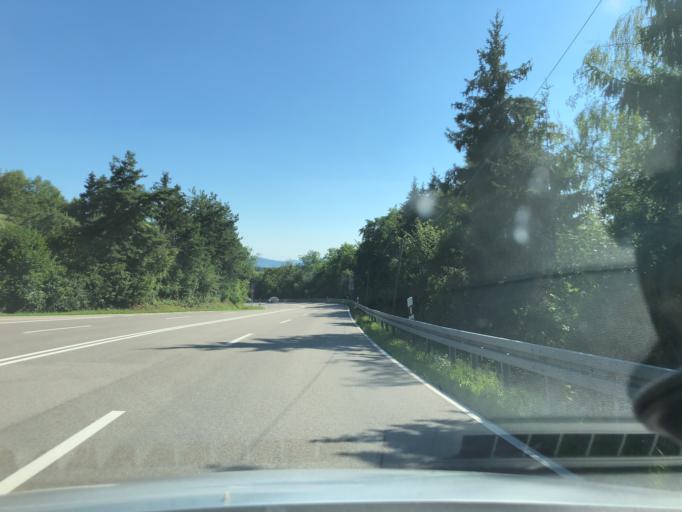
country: DE
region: Baden-Wuerttemberg
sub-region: Freiburg Region
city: Dogern
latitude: 47.6474
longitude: 8.1775
